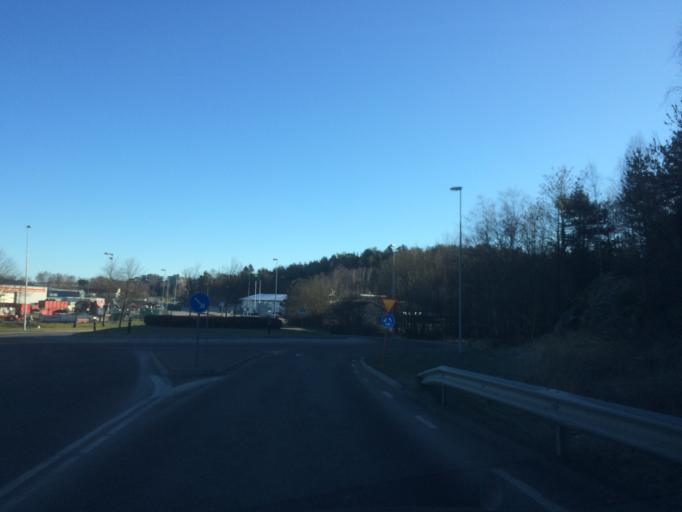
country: SE
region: Halland
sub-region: Kungsbacka Kommun
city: Kungsbacka
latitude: 57.4767
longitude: 12.0812
